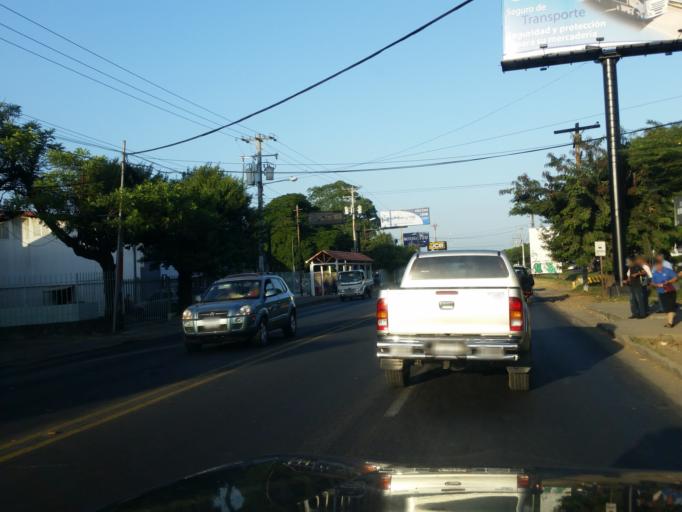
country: NI
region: Managua
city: Managua
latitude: 12.1418
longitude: -86.2946
